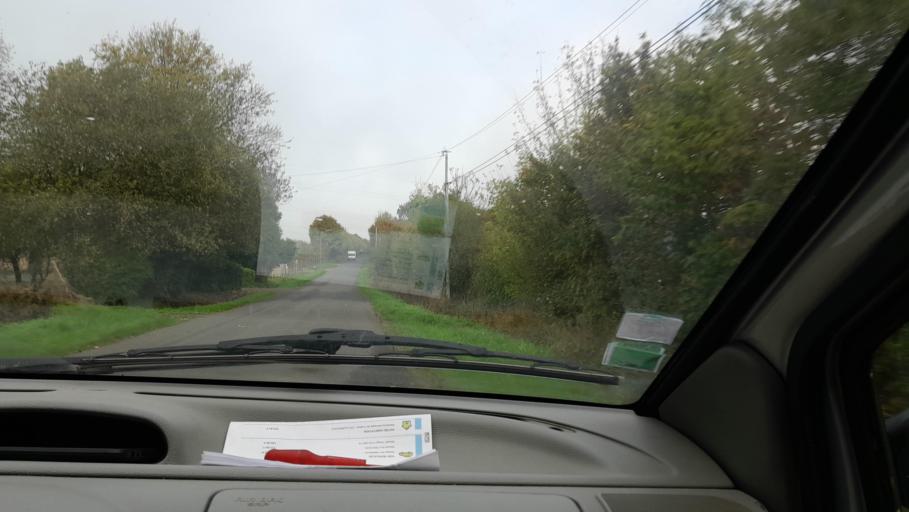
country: FR
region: Pays de la Loire
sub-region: Departement de la Mayenne
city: Saint-Pierre-la-Cour
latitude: 48.1450
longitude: -1.0310
